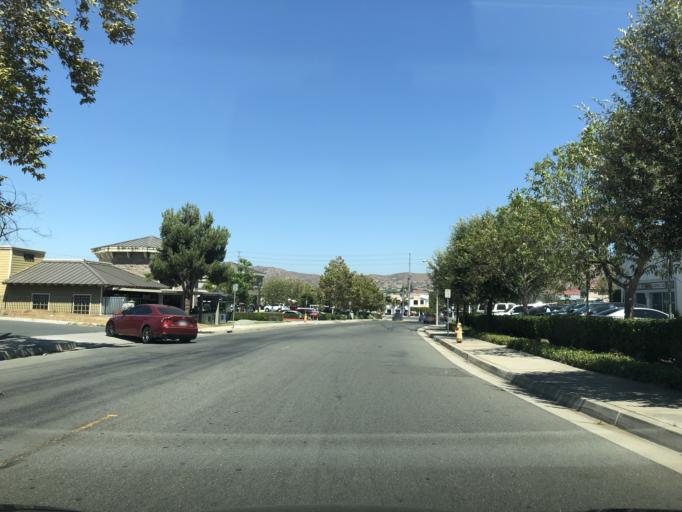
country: US
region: California
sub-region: Riverside County
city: Norco
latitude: 33.9282
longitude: -117.5601
